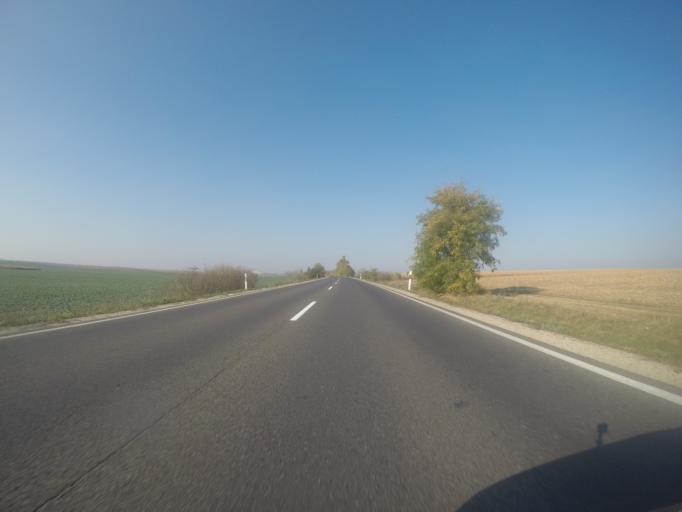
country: HU
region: Fejer
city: Racalmas
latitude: 47.0077
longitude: 18.9301
